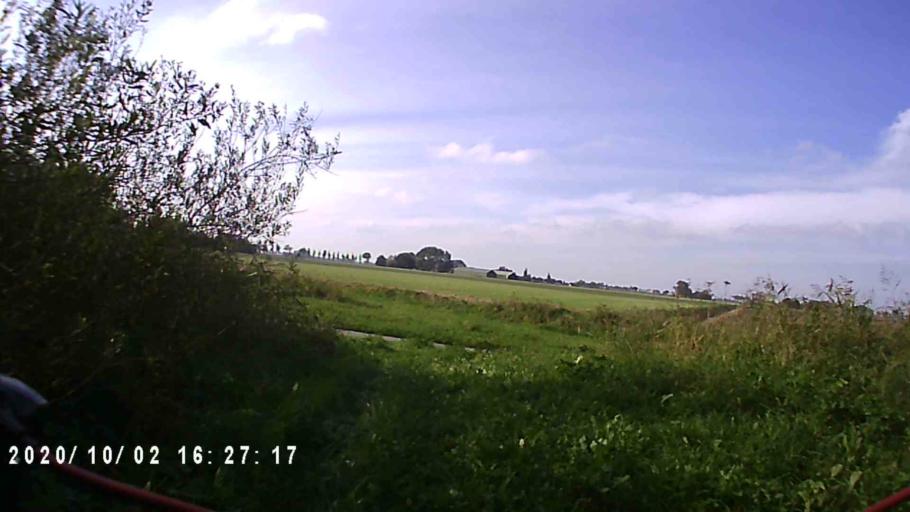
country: NL
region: Groningen
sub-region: Gemeente Zuidhorn
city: Grijpskerk
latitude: 53.2857
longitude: 6.3089
